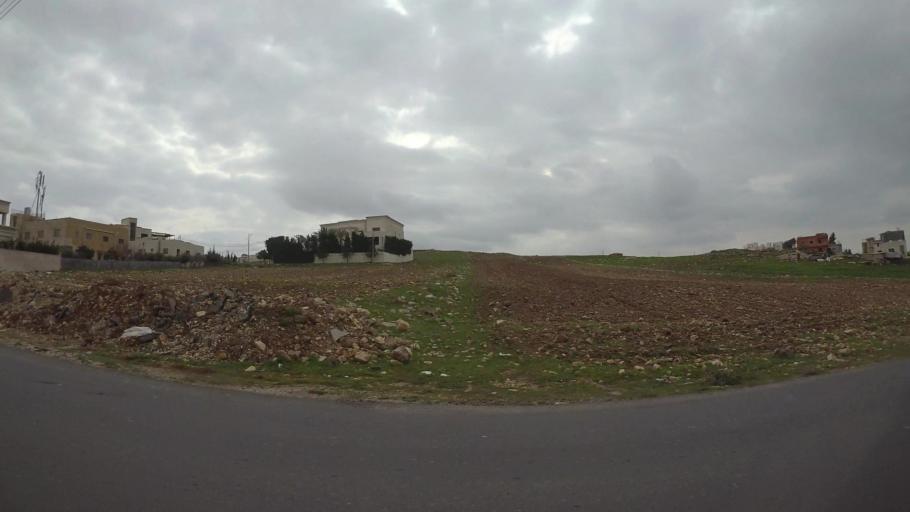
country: JO
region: Amman
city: Wadi as Sir
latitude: 31.9294
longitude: 35.8544
